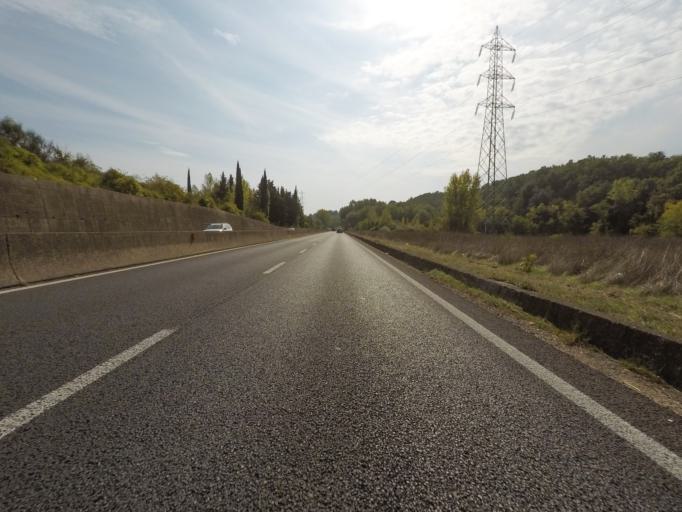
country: IT
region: Tuscany
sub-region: Provincia di Siena
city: Belverde
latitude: 43.3228
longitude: 11.2985
